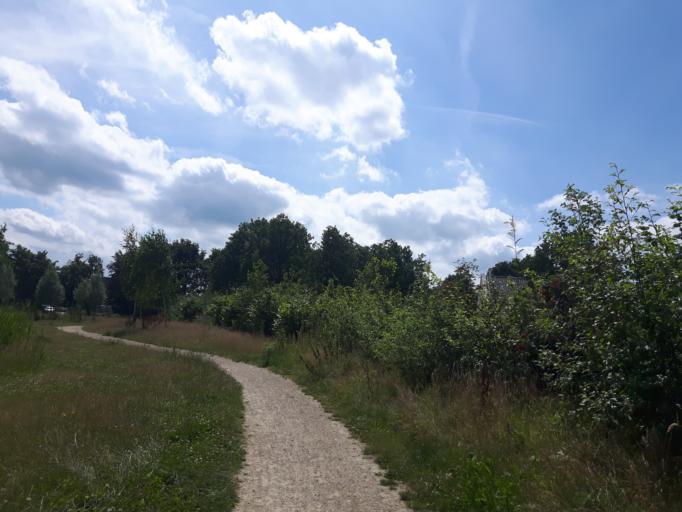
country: NL
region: Overijssel
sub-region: Gemeente Haaksbergen
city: Haaksbergen
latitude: 52.1704
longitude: 6.7505
